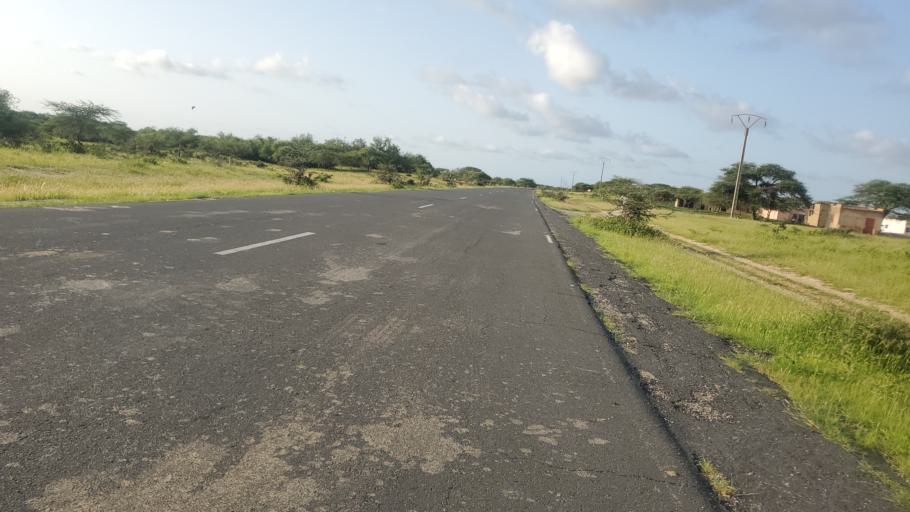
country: SN
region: Saint-Louis
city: Saint-Louis
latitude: 16.1571
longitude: -16.4100
